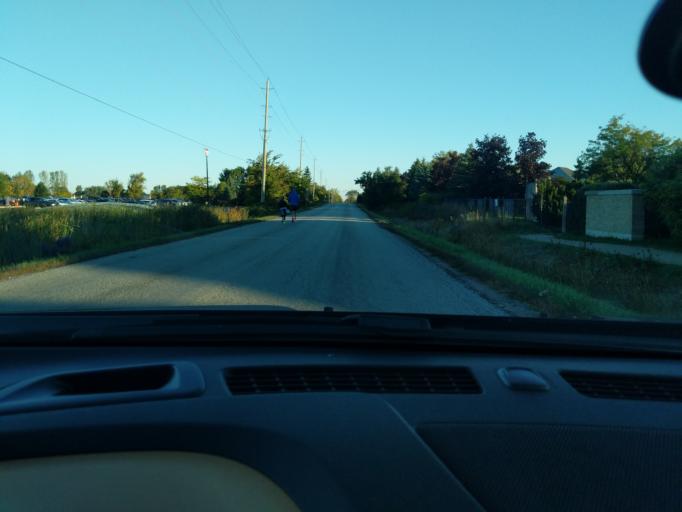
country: CA
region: Ontario
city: Collingwood
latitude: 44.4898
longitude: -80.2485
